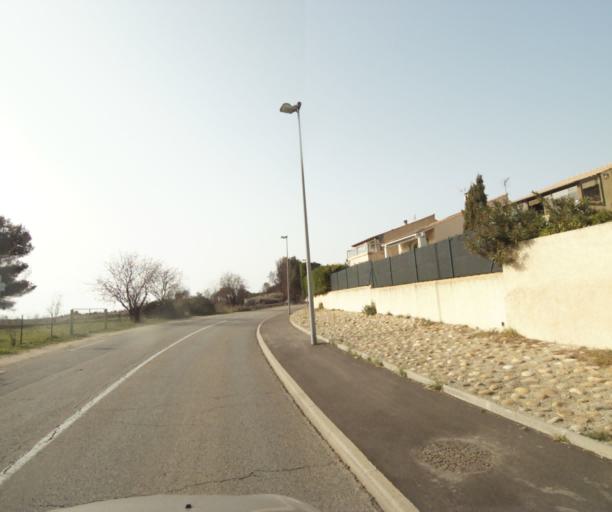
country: FR
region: Provence-Alpes-Cote d'Azur
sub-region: Departement des Bouches-du-Rhone
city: Vitrolles
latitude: 43.4617
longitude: 5.2417
